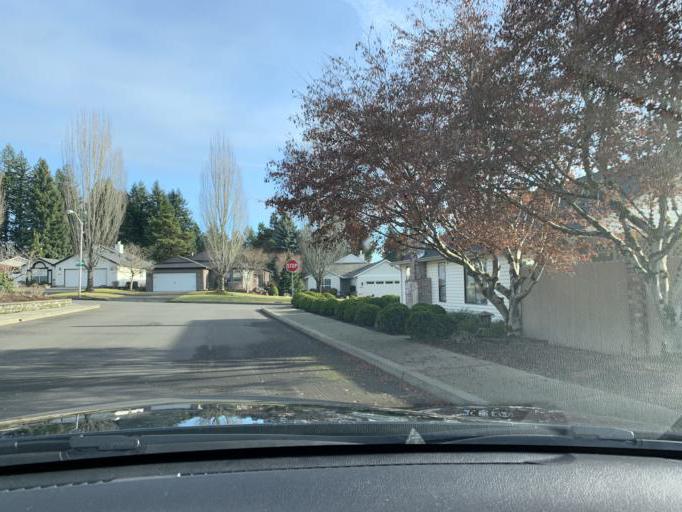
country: US
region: Washington
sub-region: Clark County
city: Mill Plain
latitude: 45.5981
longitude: -122.5119
